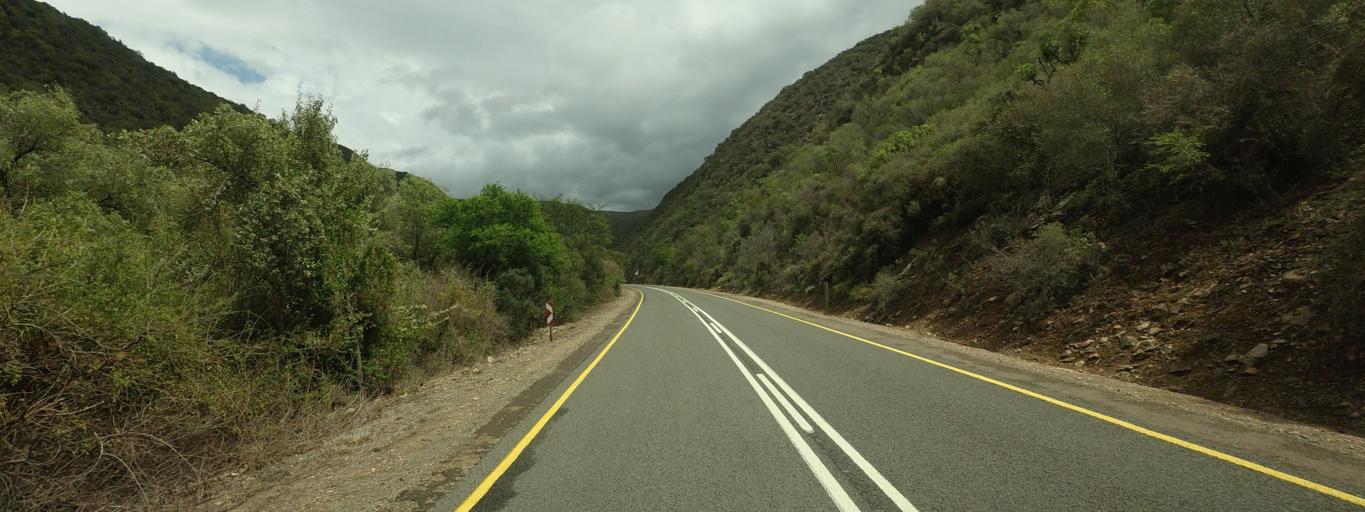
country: ZA
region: Western Cape
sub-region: Eden District Municipality
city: Oudtshoorn
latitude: -33.4503
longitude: 22.2559
